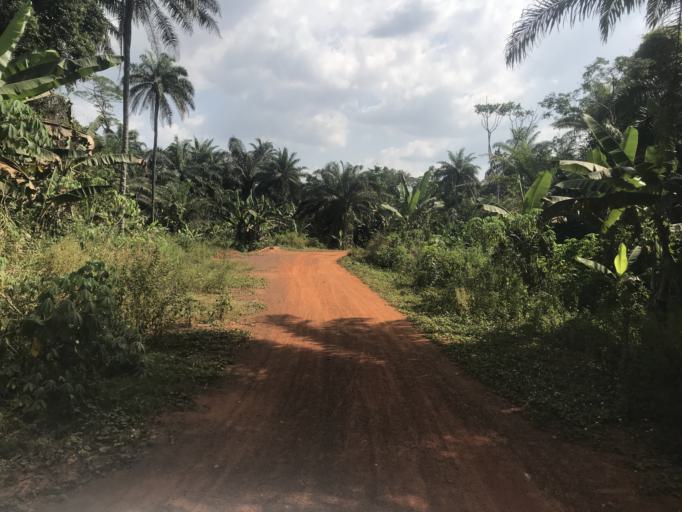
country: NG
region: Osun
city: Ibokun
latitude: 7.8176
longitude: 4.6972
